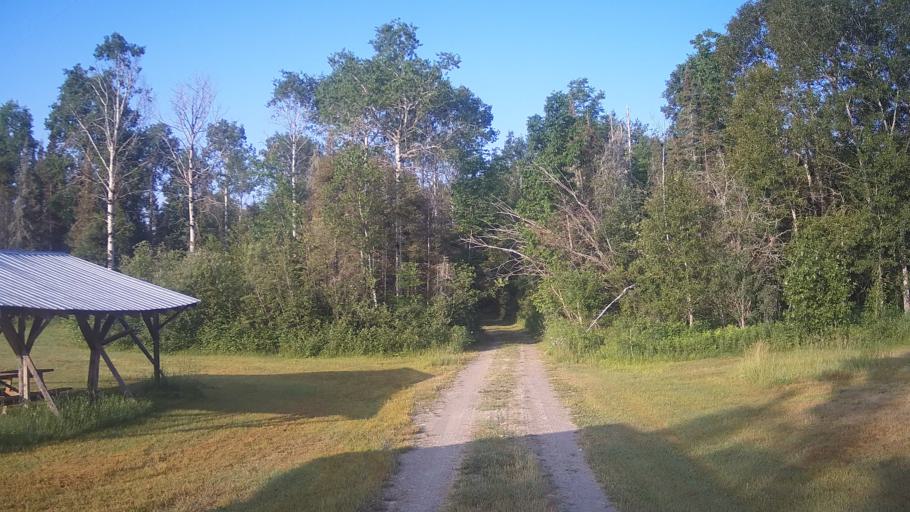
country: CA
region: Ontario
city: Rayside-Balfour
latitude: 46.5752
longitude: -81.3119
